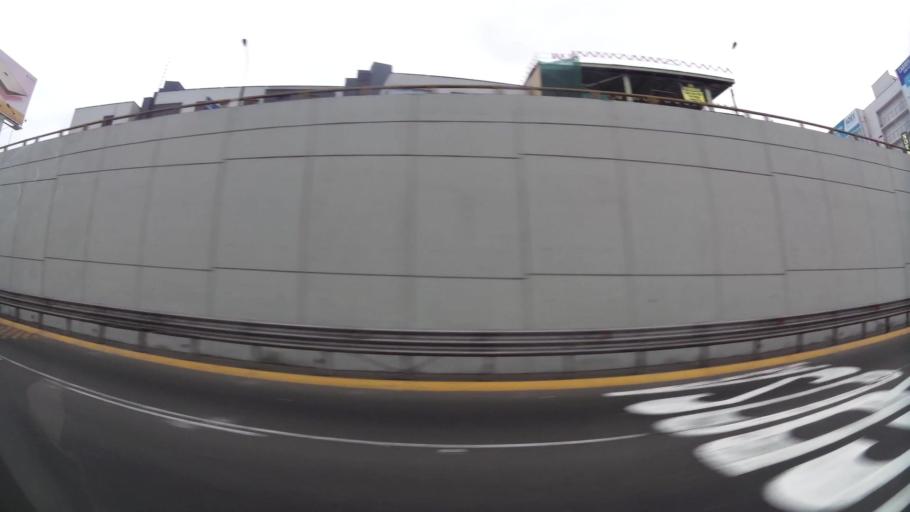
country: PE
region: Lima
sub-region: Lima
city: San Luis
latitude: -12.0866
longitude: -76.9963
